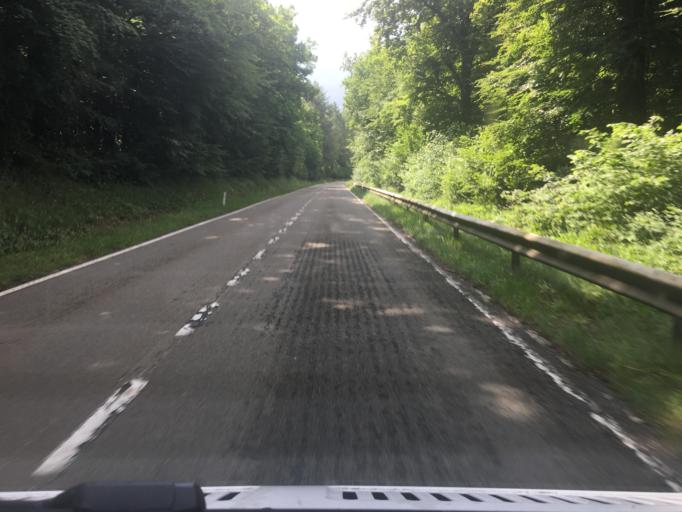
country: BE
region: Wallonia
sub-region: Province du Luxembourg
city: Florenville
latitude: 49.6416
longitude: 5.3436
